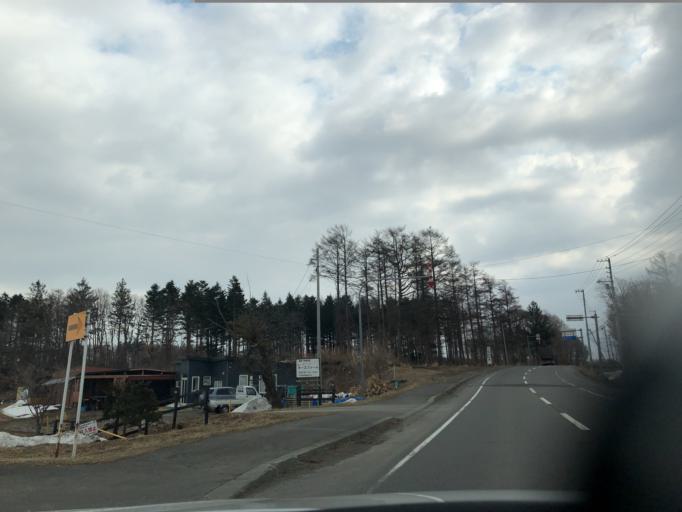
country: JP
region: Hokkaido
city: Chitose
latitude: 42.7616
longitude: 141.7756
